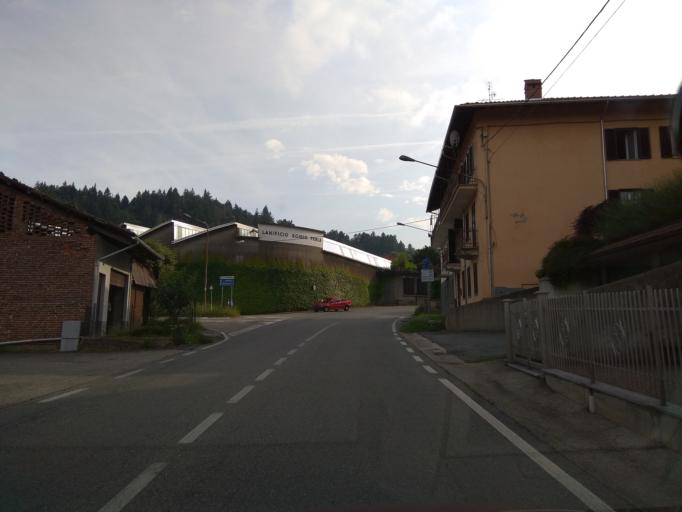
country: IT
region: Piedmont
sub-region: Provincia di Biella
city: Trivero-Prativero-Ponzone
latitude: 45.6446
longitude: 8.1712
